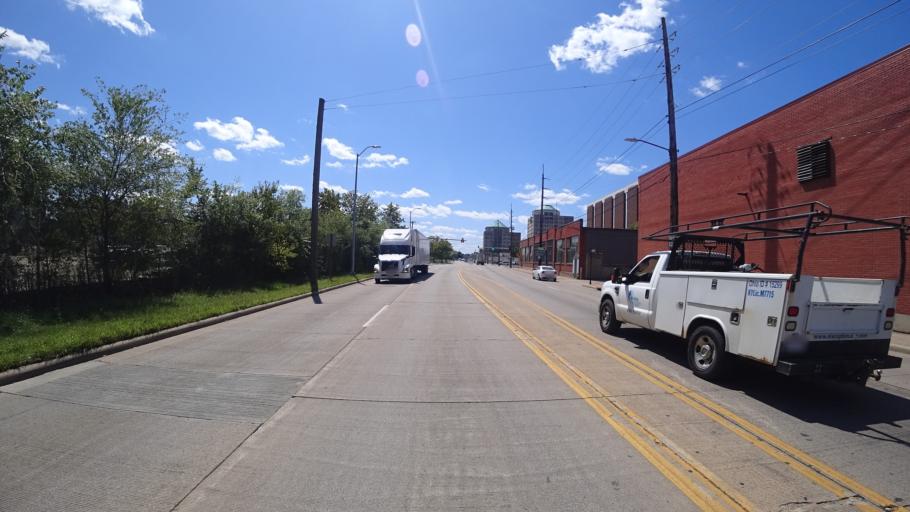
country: US
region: Ohio
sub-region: Butler County
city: Hamilton
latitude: 39.4015
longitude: -84.5583
